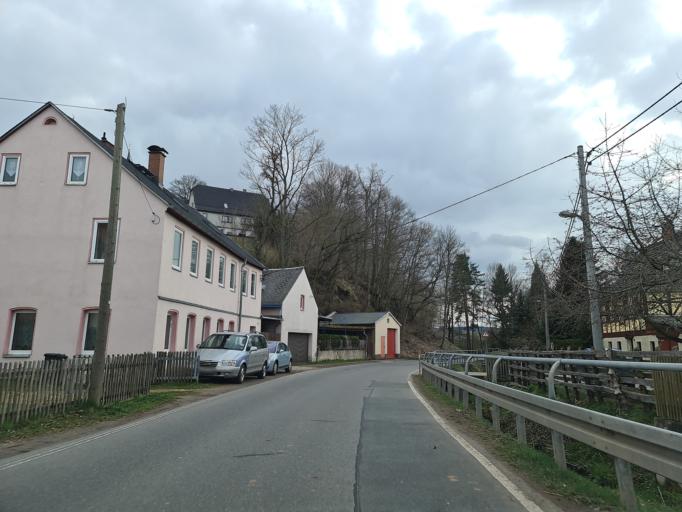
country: DE
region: Saxony
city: Wildenfels
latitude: 50.6760
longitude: 12.6086
